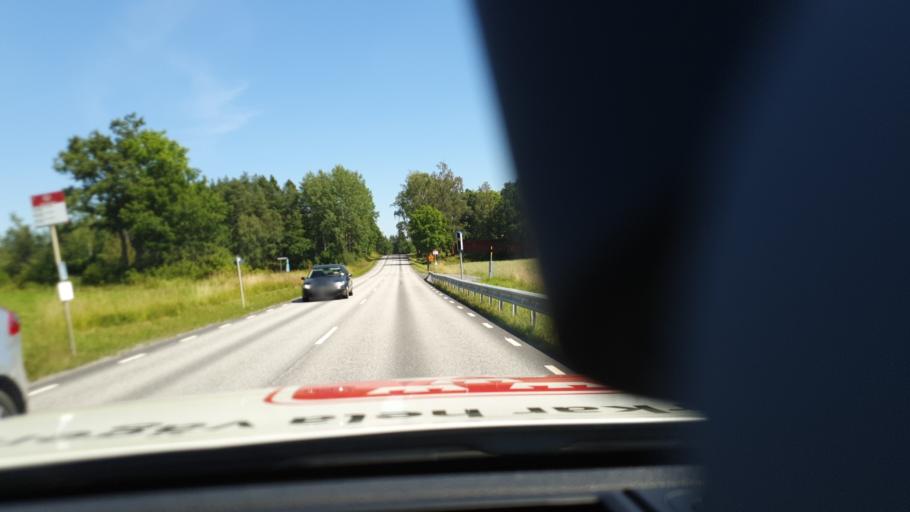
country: SE
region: Stockholm
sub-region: Norrtalje Kommun
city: Norrtalje
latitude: 59.7771
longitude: 18.7599
